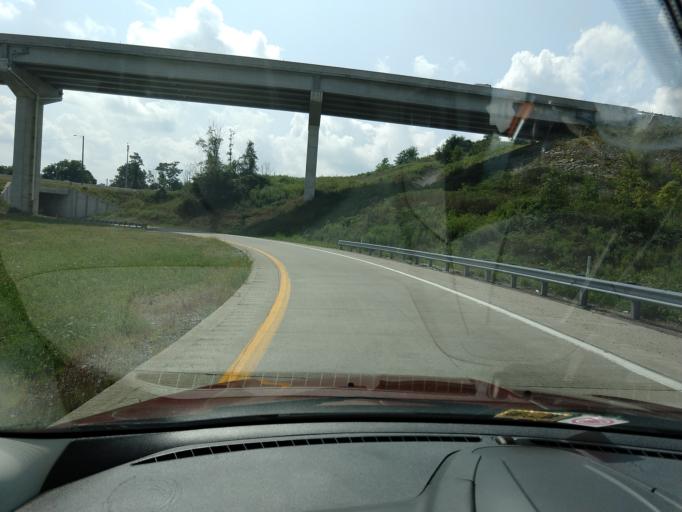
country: US
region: Pennsylvania
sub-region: Washington County
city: East Washington
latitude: 40.1634
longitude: -80.1930
